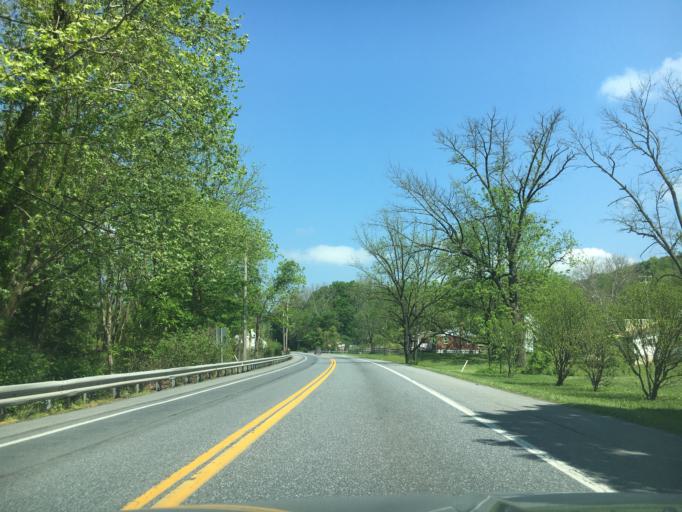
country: US
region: Pennsylvania
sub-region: Berks County
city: New Berlinville
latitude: 40.3529
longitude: -75.6628
